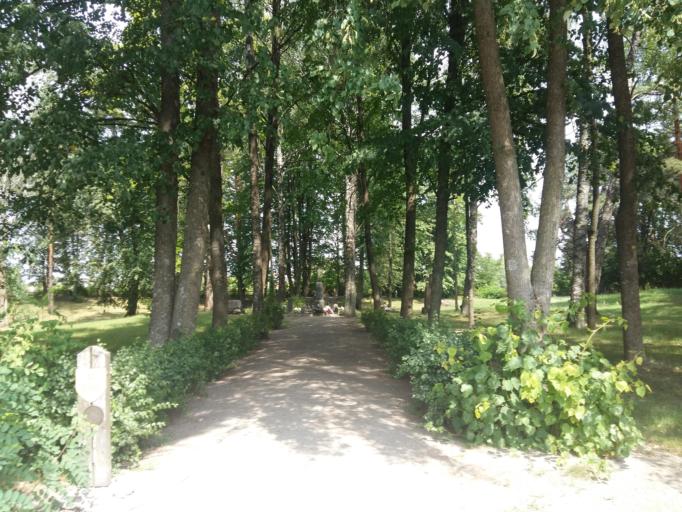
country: LT
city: Veisiejai
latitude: 54.0033
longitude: 23.6636
